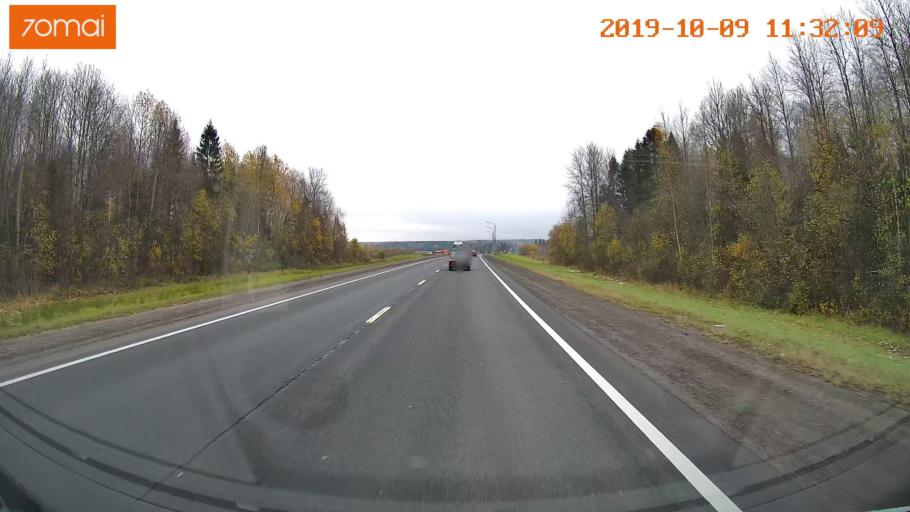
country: RU
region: Vologda
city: Gryazovets
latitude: 59.0387
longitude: 40.1060
